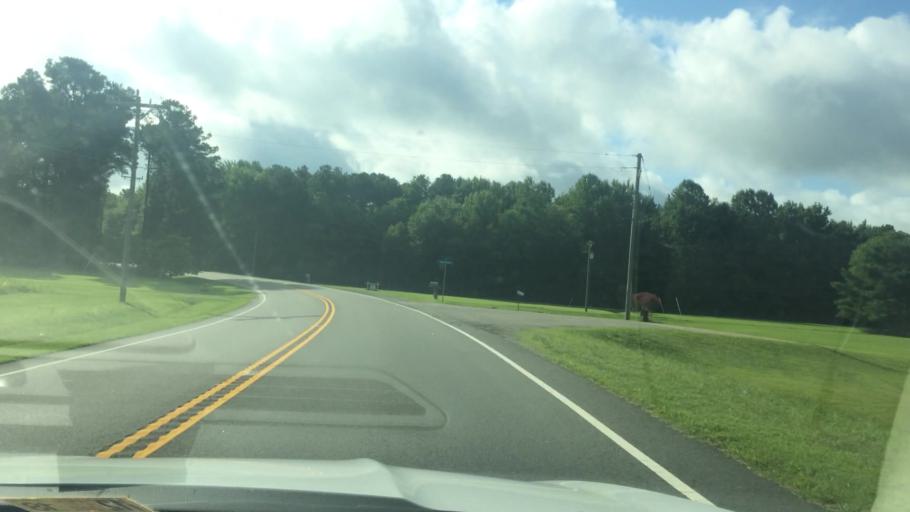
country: US
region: Virginia
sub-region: Middlesex County
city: Deltaville
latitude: 37.4911
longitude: -76.4345
